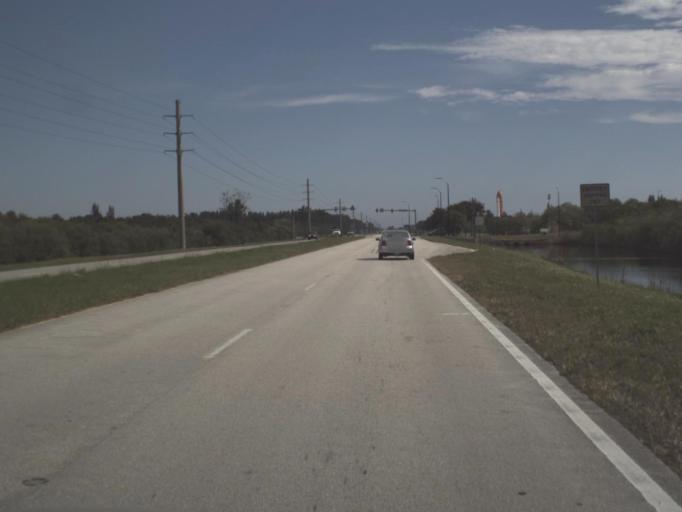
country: US
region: Florida
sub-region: Brevard County
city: Merritt Island
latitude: 28.5262
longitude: -80.6952
